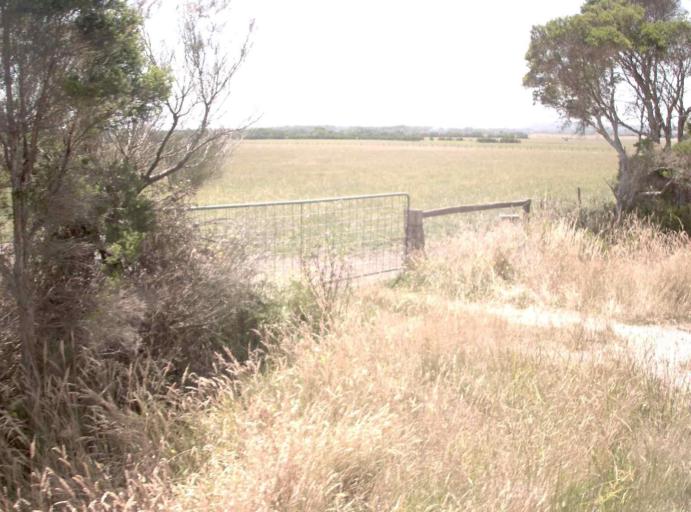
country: AU
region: Victoria
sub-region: Bass Coast
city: North Wonthaggi
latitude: -38.6672
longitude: 145.9671
